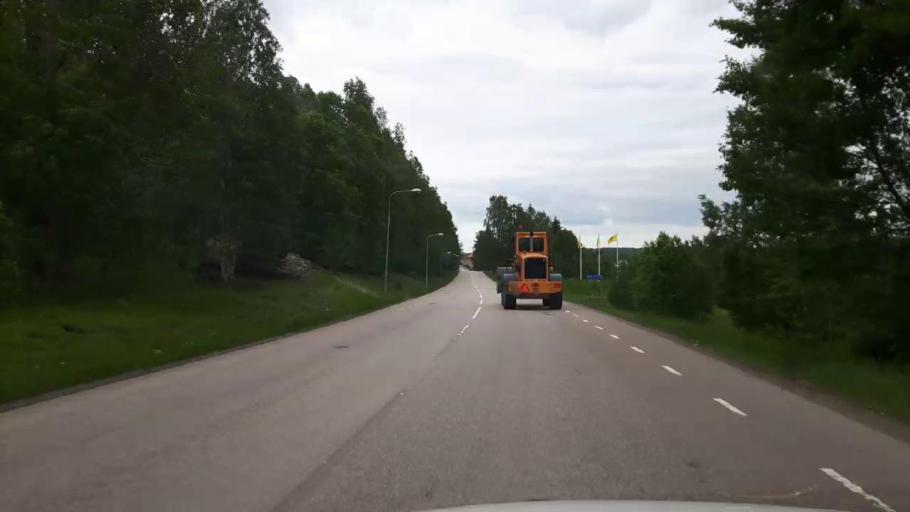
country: SE
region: Vaestmanland
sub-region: Kopings Kommun
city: Kolsva
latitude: 59.6085
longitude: 15.8292
